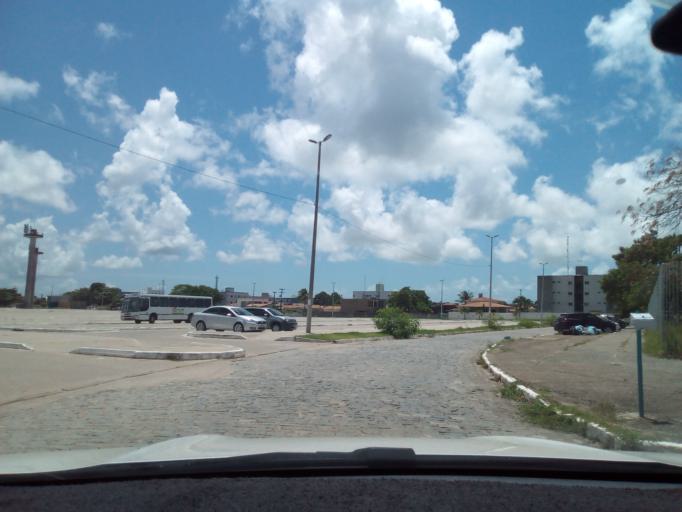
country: BR
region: Paraiba
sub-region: Joao Pessoa
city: Joao Pessoa
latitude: -7.1692
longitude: -34.8719
